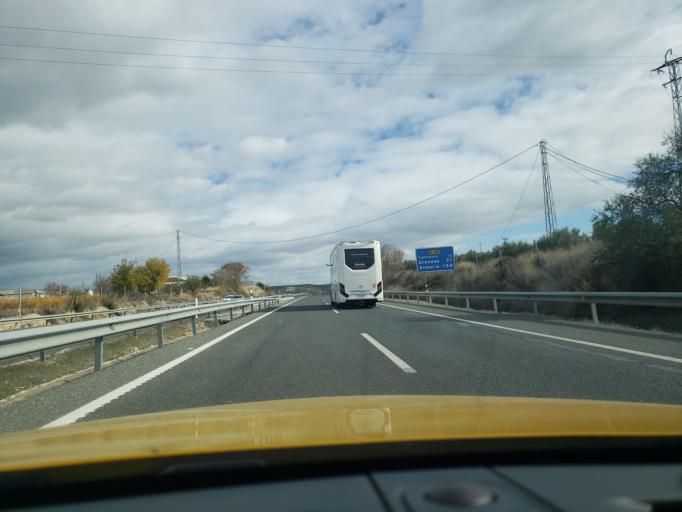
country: ES
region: Andalusia
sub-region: Provincia de Granada
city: Villanueva de Mesia
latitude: 37.1952
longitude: -4.0173
